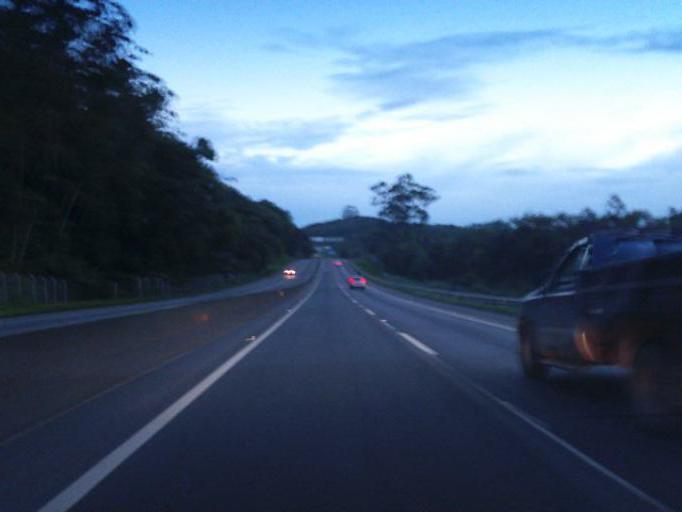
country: BR
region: Santa Catarina
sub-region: Joinville
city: Joinville
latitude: -26.4211
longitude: -48.8306
